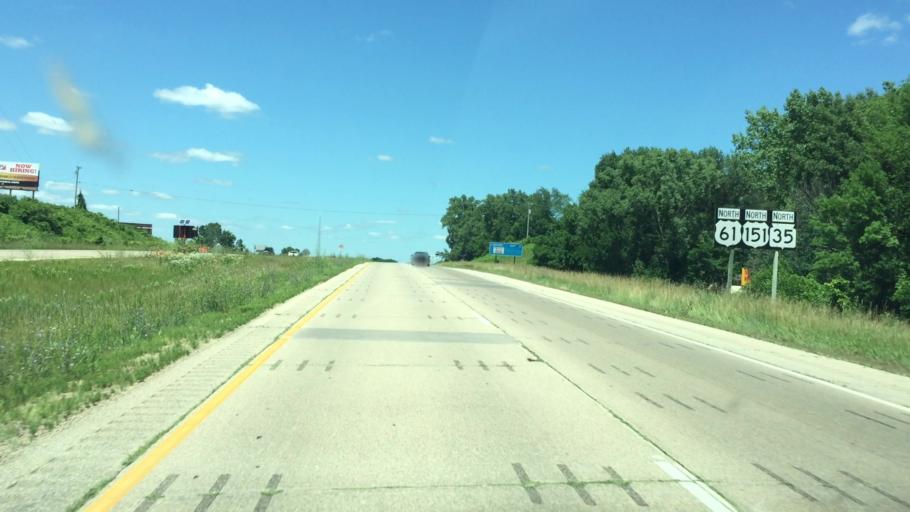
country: US
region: Illinois
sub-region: Jo Daviess County
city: East Dubuque
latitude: 42.5268
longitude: -90.6137
